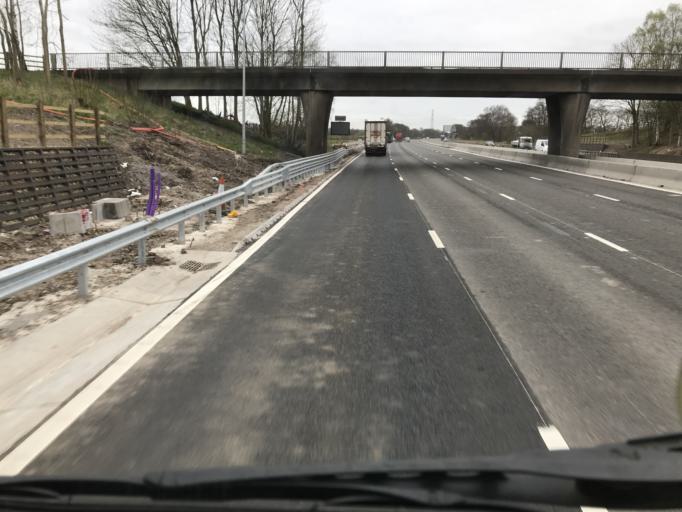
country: GB
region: England
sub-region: City and Borough of Salford
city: Irlam
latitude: 53.4727
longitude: -2.4011
